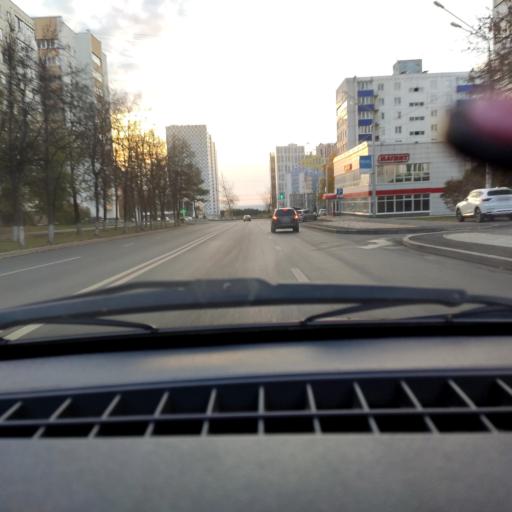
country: RU
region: Bashkortostan
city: Ufa
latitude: 54.7678
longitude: 56.0265
